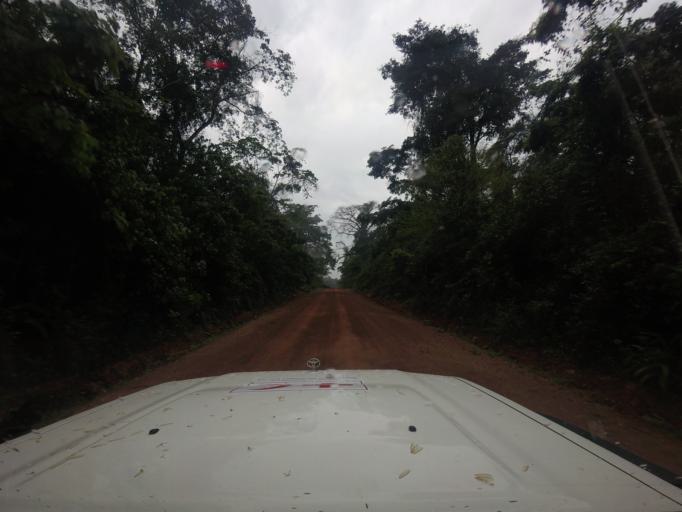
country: LR
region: Lofa
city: Voinjama
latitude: 8.3855
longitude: -9.8269
